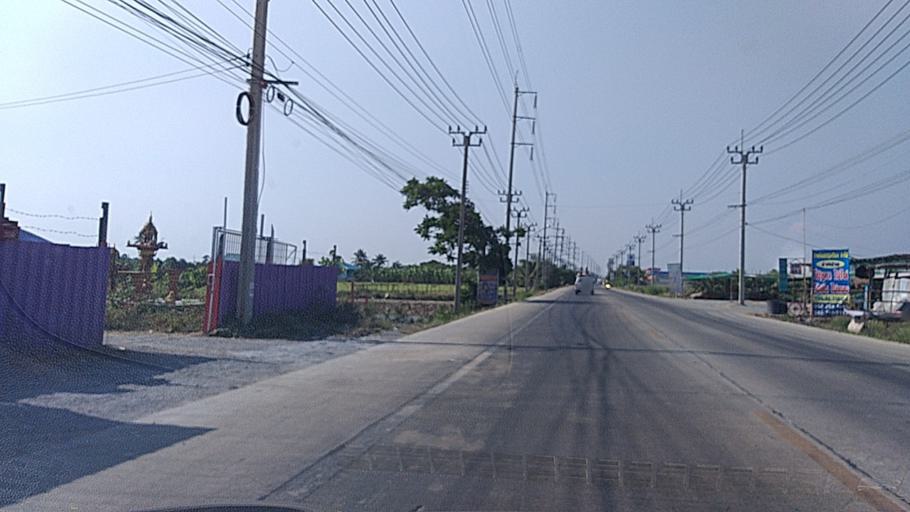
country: TH
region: Nonthaburi
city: Bang Yai
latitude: 13.9005
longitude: 100.3247
